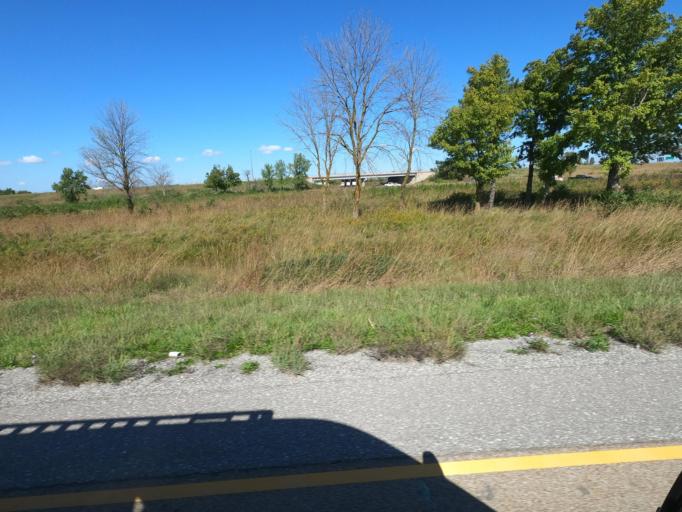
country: US
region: Illinois
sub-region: Washington County
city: Okawville
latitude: 38.4381
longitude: -89.5296
